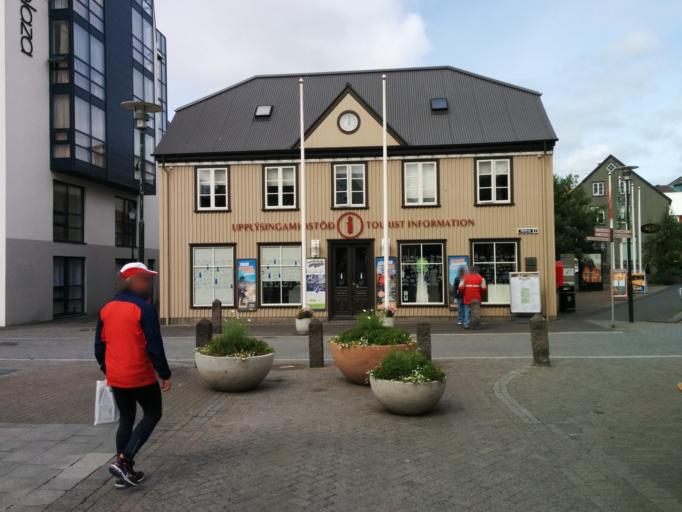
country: IS
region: Capital Region
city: Kopavogur
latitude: 64.1484
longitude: -21.9411
